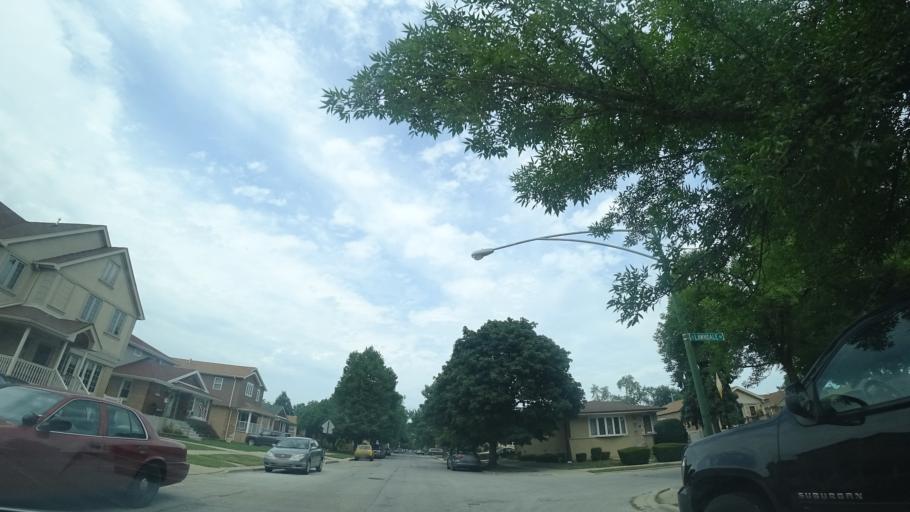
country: US
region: Illinois
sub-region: Cook County
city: Merrionette Park
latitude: 41.6977
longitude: -87.7132
